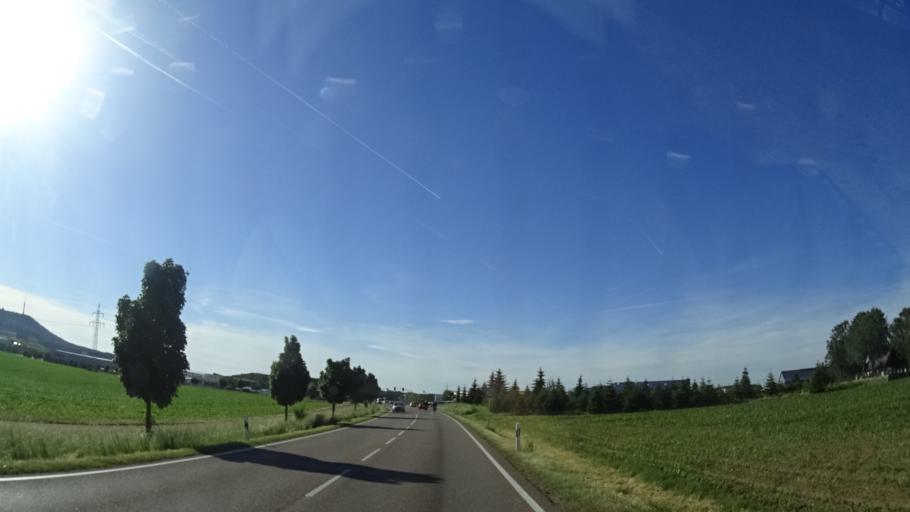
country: DE
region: Baden-Wuerttemberg
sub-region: Regierungsbezirk Stuttgart
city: Untermunkheim
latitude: 49.1753
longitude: 9.7117
